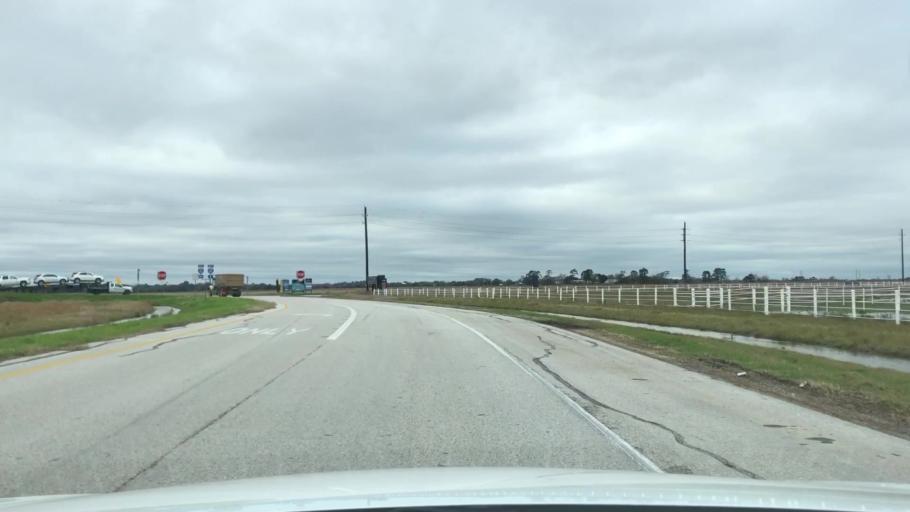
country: US
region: Texas
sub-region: Waller County
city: Brookshire
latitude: 29.7786
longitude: -95.9191
